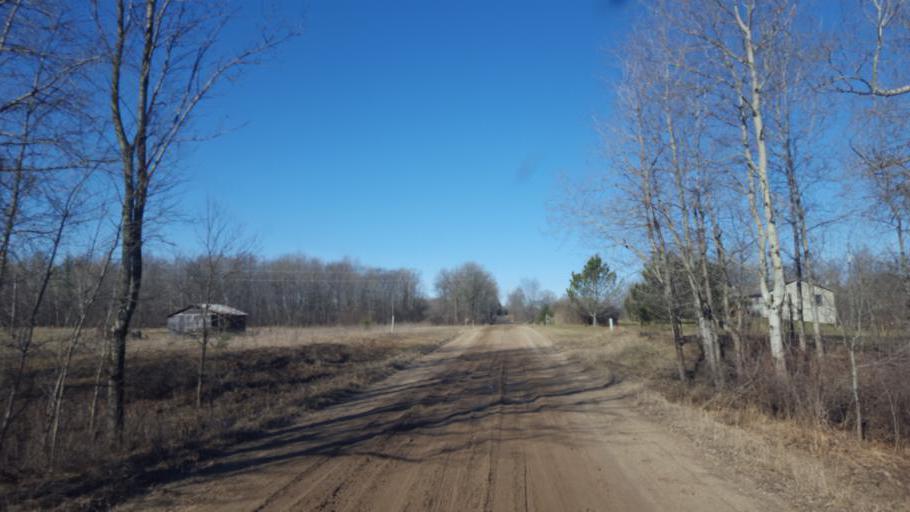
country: US
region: Michigan
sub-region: Isabella County
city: Lake Isabella
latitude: 43.5383
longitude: -85.0185
